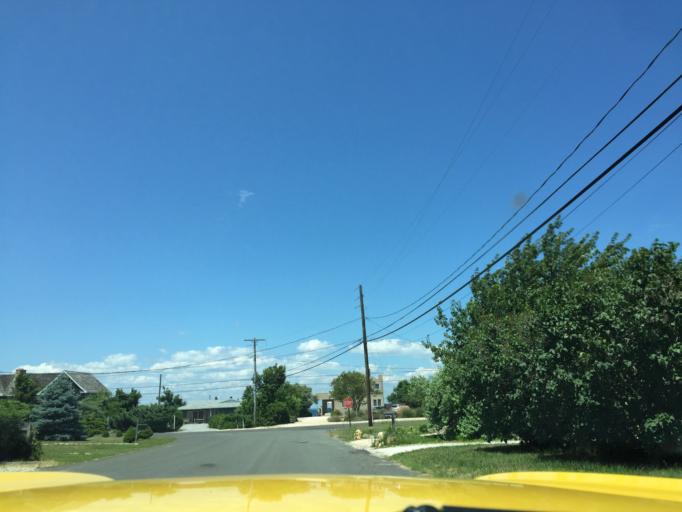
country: US
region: New York
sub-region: Suffolk County
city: Montauk
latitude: 41.0713
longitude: -71.9502
